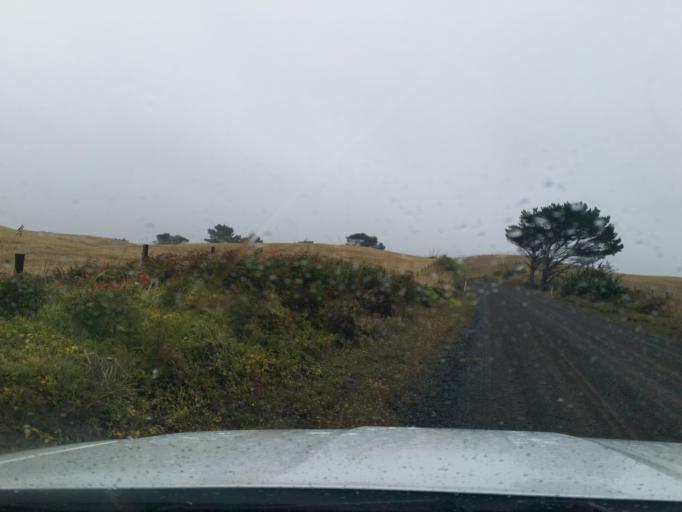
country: NZ
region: Northland
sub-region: Kaipara District
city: Dargaville
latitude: -36.0587
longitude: 173.8682
